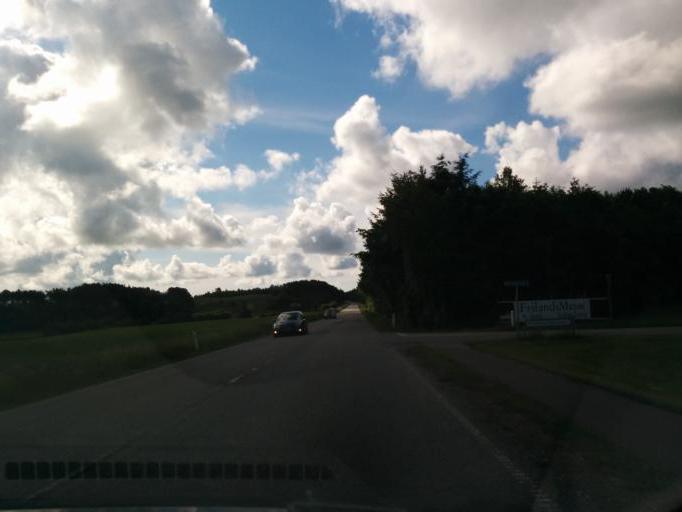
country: DK
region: Central Jutland
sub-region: Syddjurs Kommune
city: Ronde
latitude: 56.2826
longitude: 10.5882
